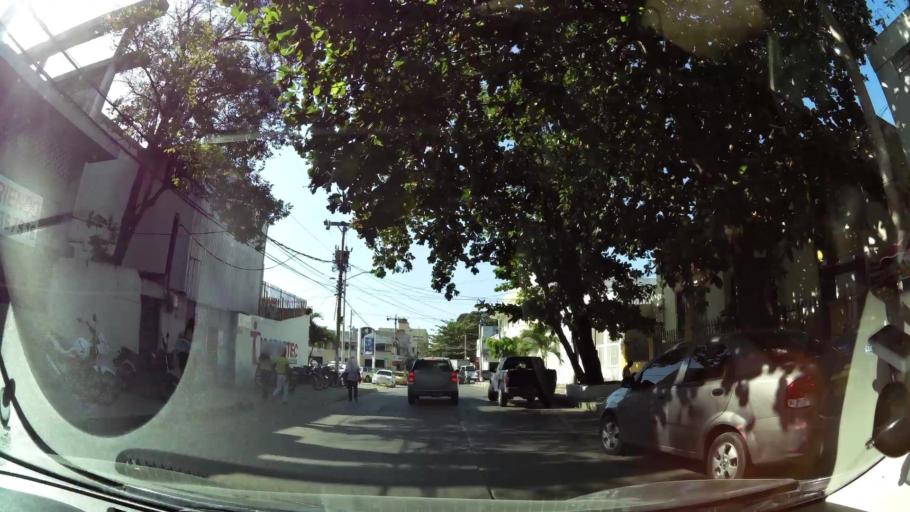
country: CO
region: Atlantico
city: Barranquilla
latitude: 10.9838
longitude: -74.7871
